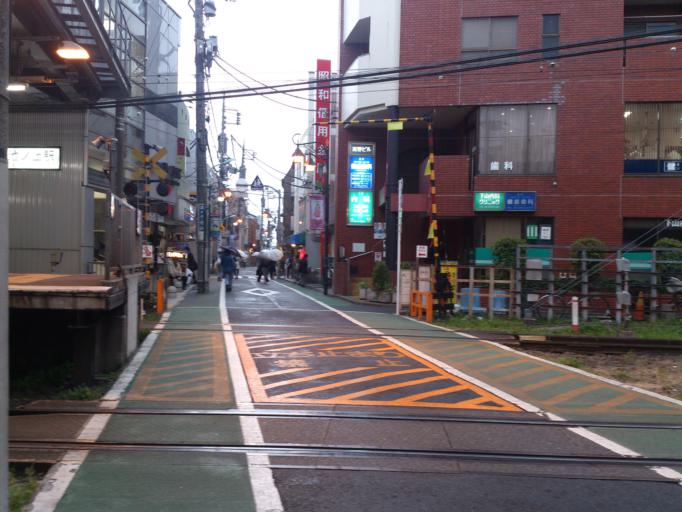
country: JP
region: Tokyo
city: Tokyo
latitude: 35.6606
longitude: 139.6728
